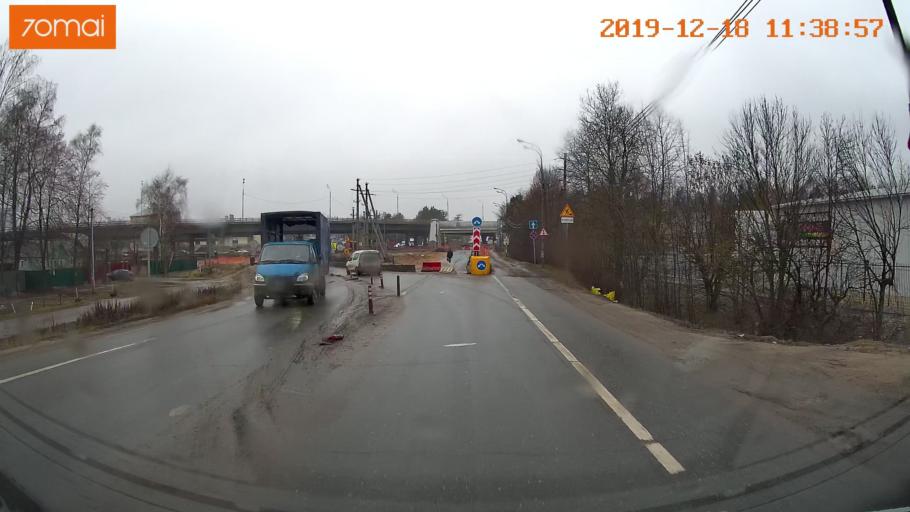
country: RU
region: Moskovskaya
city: Zvenigorod
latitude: 55.6993
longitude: 36.8838
